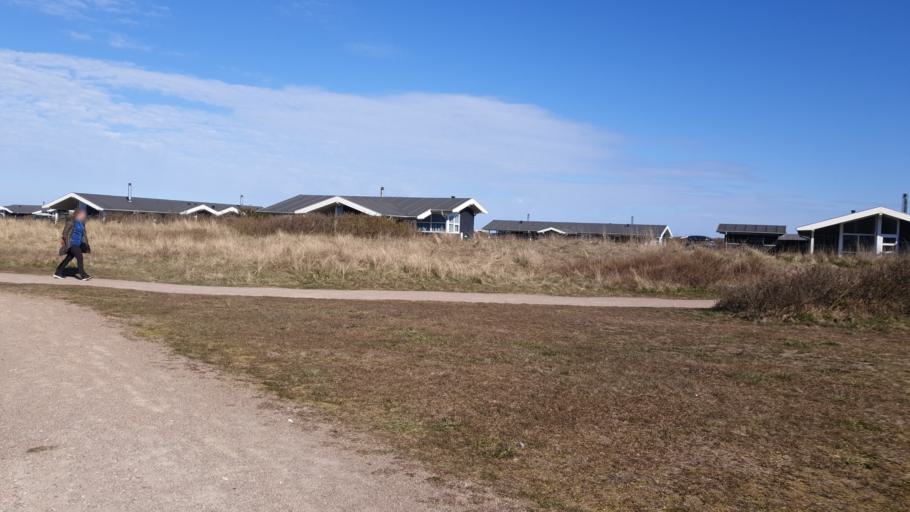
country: DK
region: North Denmark
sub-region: Hjorring Kommune
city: Hjorring
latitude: 57.4932
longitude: 9.8349
